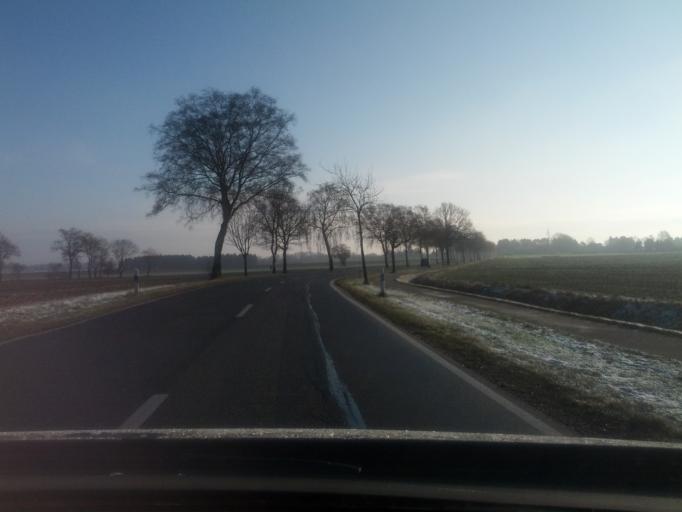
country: DE
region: Lower Saxony
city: Dohren
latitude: 53.2913
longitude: 9.6922
